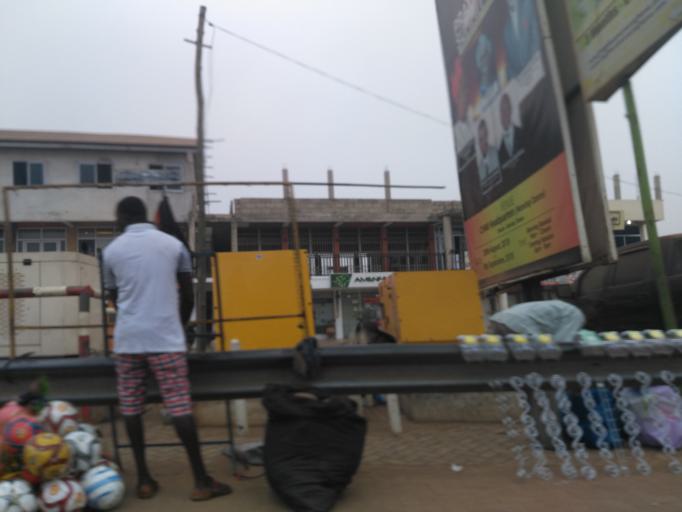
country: GH
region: Ashanti
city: Kumasi
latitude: 6.7087
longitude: -1.6364
